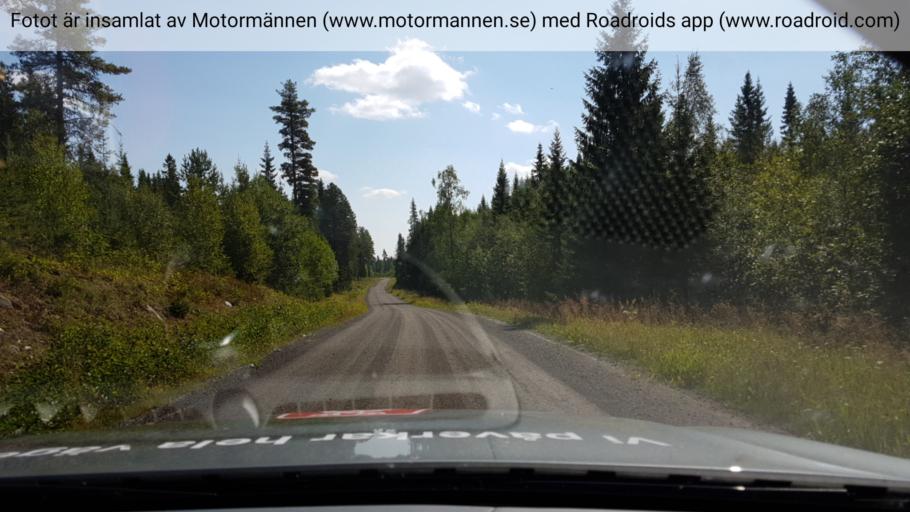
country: SE
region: Jaemtland
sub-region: OEstersunds Kommun
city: Lit
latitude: 63.3492
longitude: 15.2560
